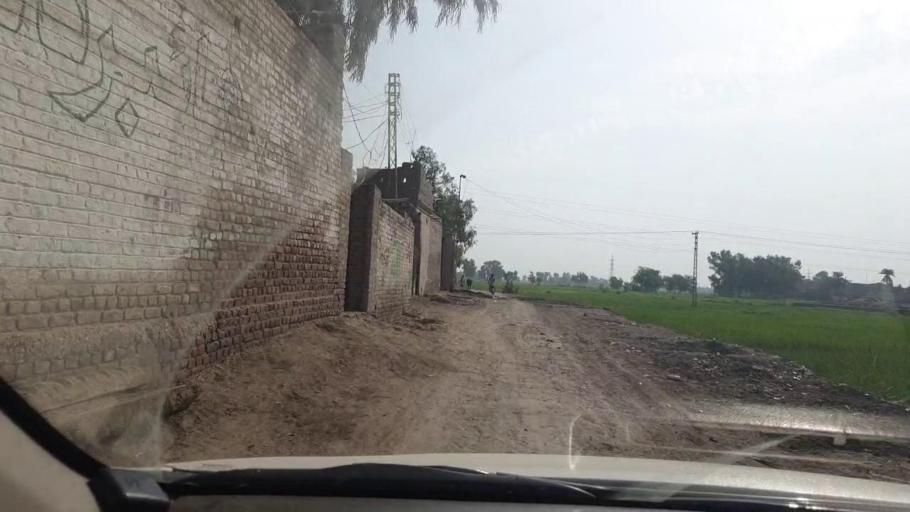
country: PK
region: Sindh
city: Lakhi
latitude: 27.8257
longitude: 68.7323
